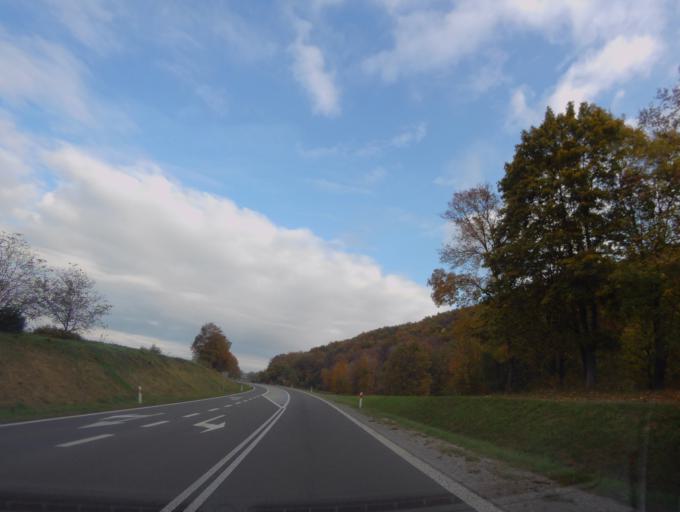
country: PL
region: Lublin Voivodeship
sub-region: Powiat bilgorajski
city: Goraj
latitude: 50.7551
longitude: 22.6720
